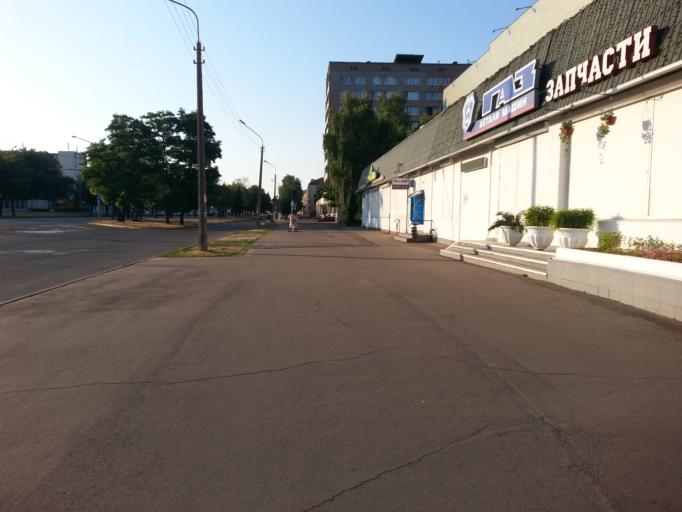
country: BY
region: Minsk
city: Vyaliki Trastsyanets
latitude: 53.8720
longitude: 27.6395
